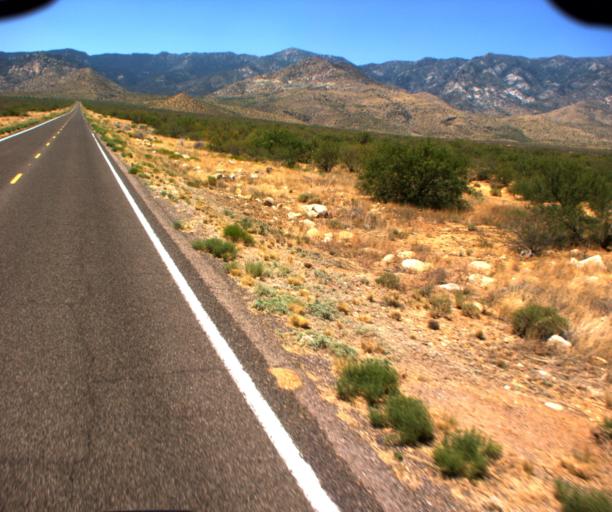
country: US
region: Arizona
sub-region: Graham County
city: Swift Trail Junction
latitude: 32.7070
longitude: -109.7372
